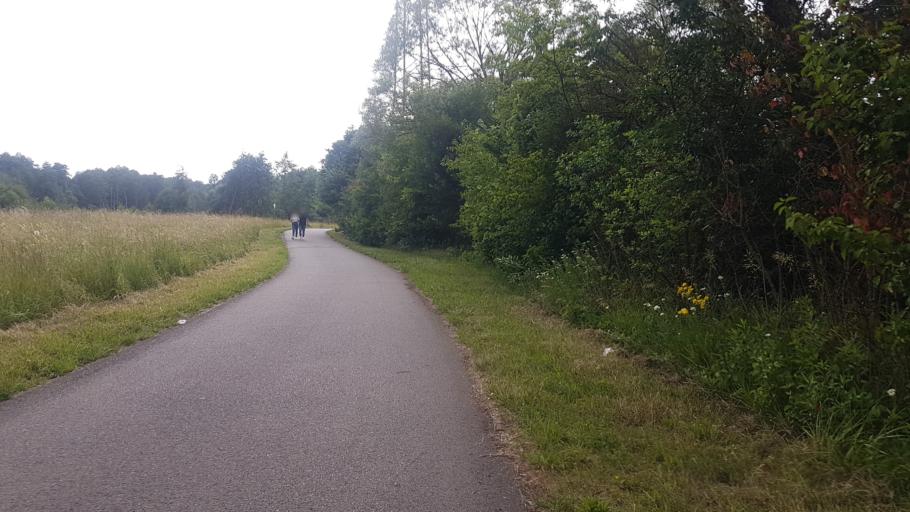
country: DE
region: Saarland
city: Wadgassen
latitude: 49.2737
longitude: 6.7863
